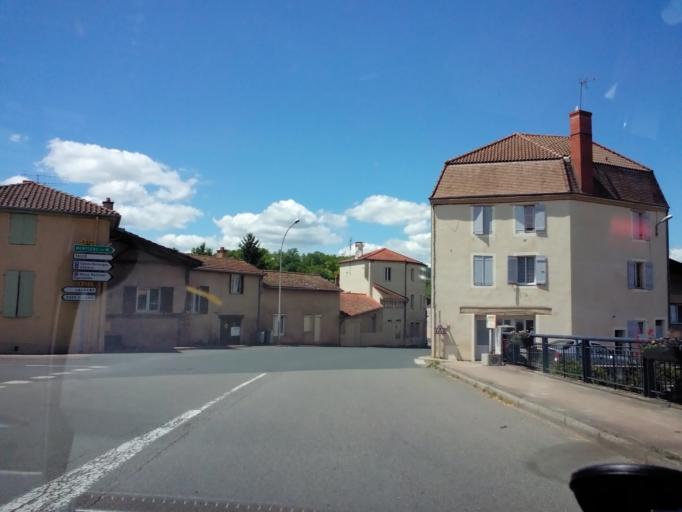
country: FR
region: Bourgogne
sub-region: Departement de Saone-et-Loire
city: Cluny
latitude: 46.4255
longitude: 4.6652
